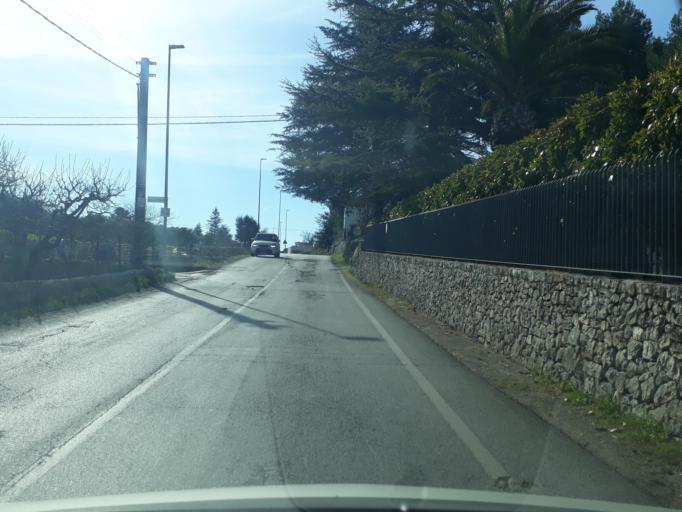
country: IT
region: Apulia
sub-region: Provincia di Brindisi
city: Lamie di Olimpie-Selva
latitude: 40.7899
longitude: 17.3578
